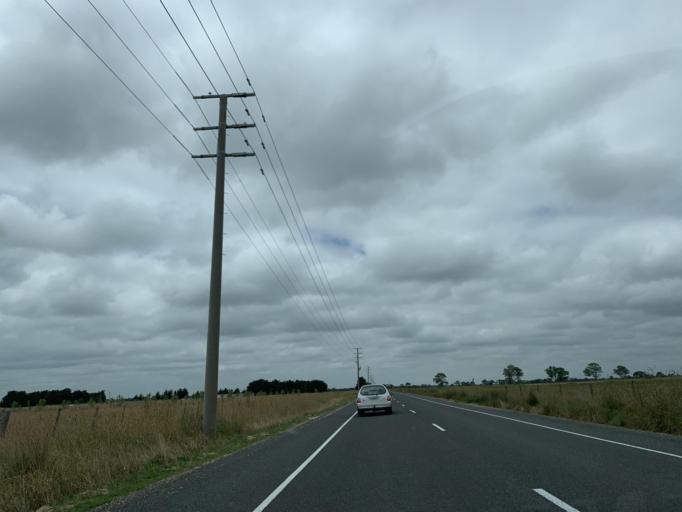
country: AU
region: Victoria
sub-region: Wellington
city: Heyfield
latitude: -37.9878
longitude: 146.8590
